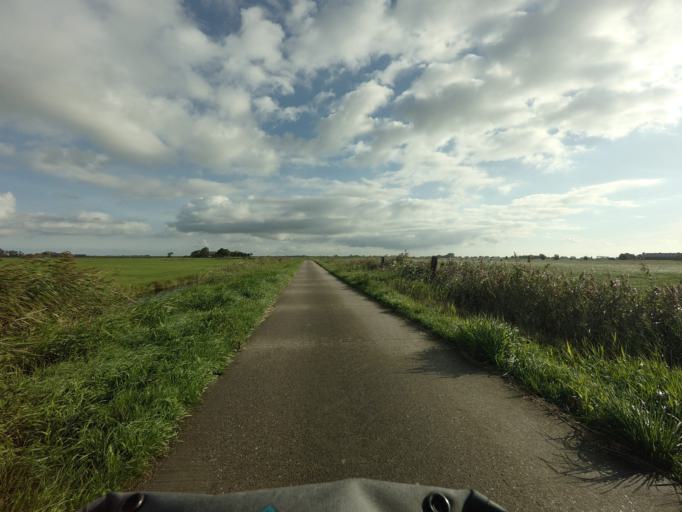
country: NL
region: Friesland
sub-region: Sudwest Fryslan
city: Workum
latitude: 53.0270
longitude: 5.4624
